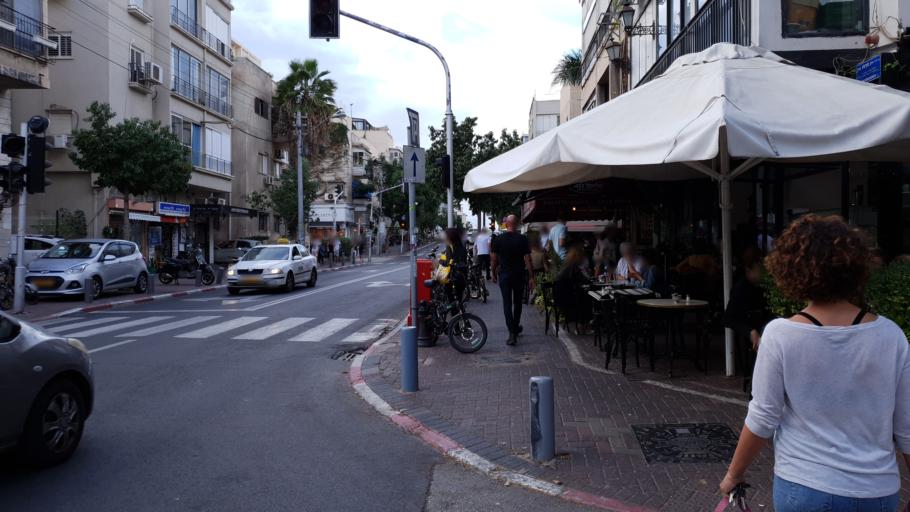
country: IL
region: Tel Aviv
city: Tel Aviv
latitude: 32.0768
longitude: 34.7702
